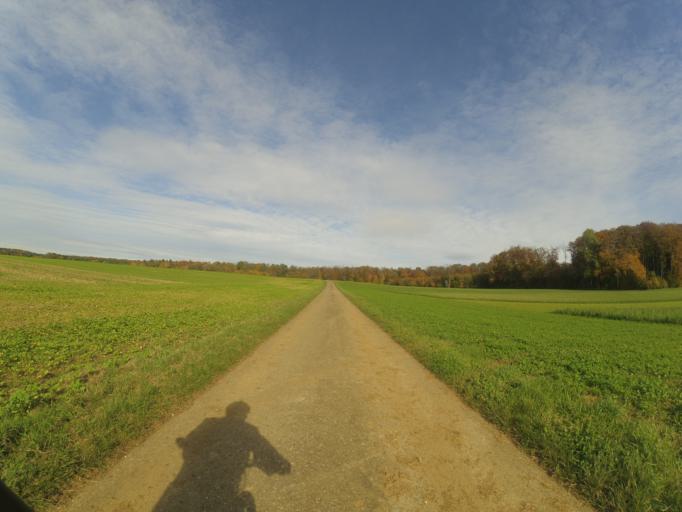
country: DE
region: Baden-Wuerttemberg
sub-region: Tuebingen Region
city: Amstetten
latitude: 48.6004
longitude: 9.9184
